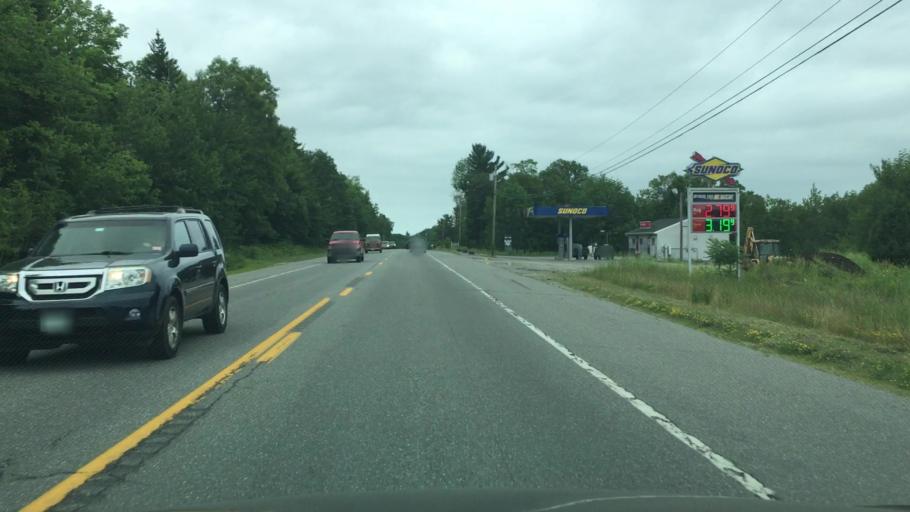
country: US
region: Maine
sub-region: Waldo County
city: Stockton Springs
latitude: 44.4944
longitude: -68.8425
